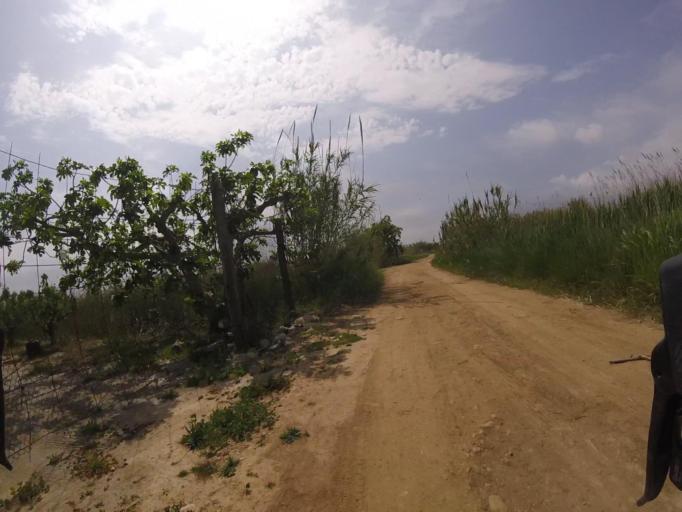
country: ES
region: Valencia
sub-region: Provincia de Castello
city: Orpesa/Oropesa del Mar
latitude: 40.1571
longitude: 0.1723
